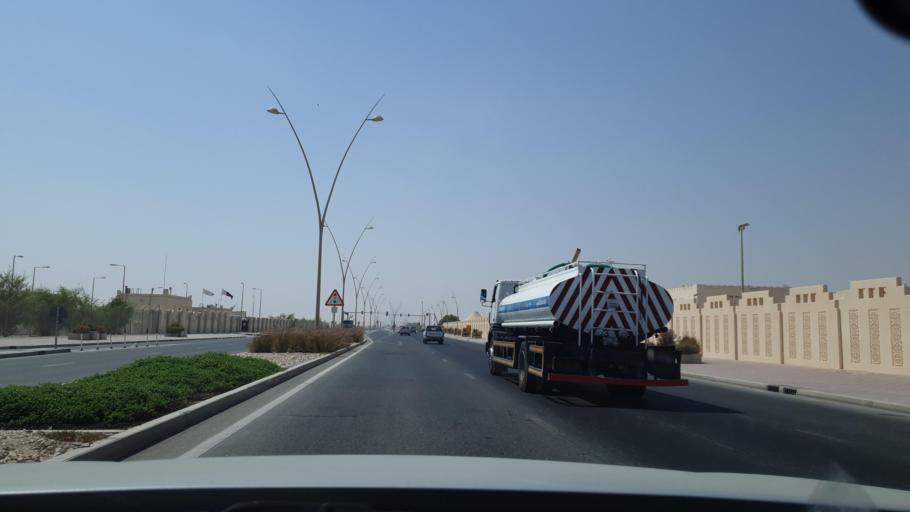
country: QA
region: Al Khawr
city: Al Khawr
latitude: 25.6715
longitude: 51.4835
